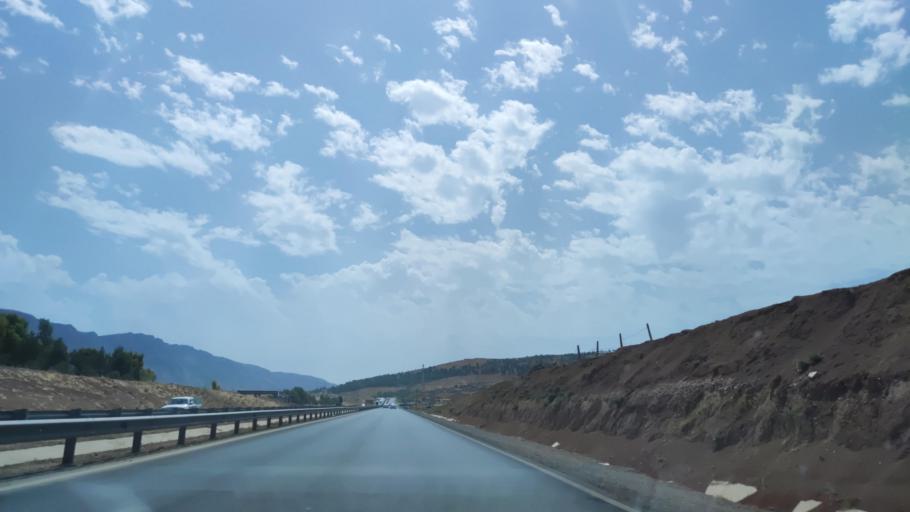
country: IQ
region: Arbil
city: Shaqlawah
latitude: 36.5009
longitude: 44.3580
